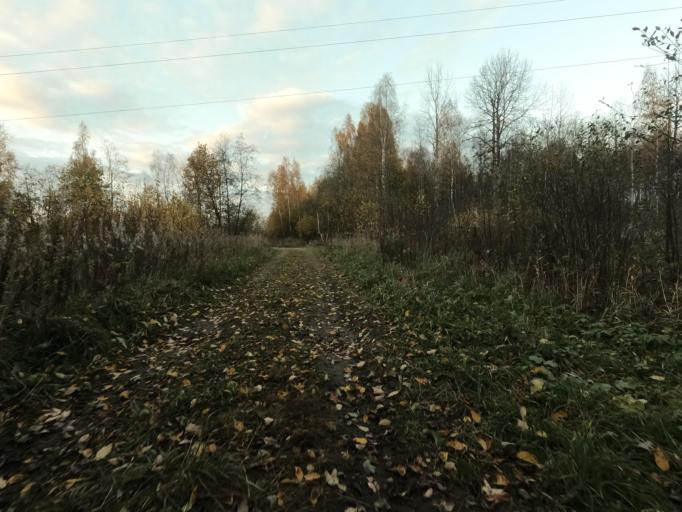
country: RU
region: Leningrad
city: Mga
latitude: 59.8230
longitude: 31.1779
